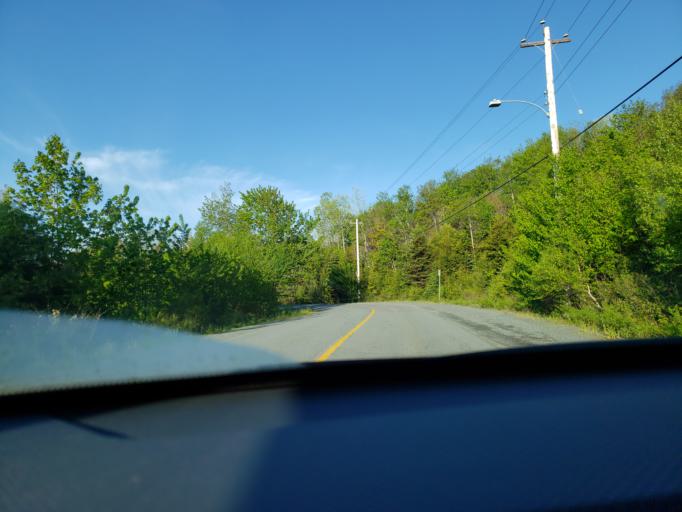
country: CA
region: Nova Scotia
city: Cole Harbour
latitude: 44.7419
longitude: -63.3802
